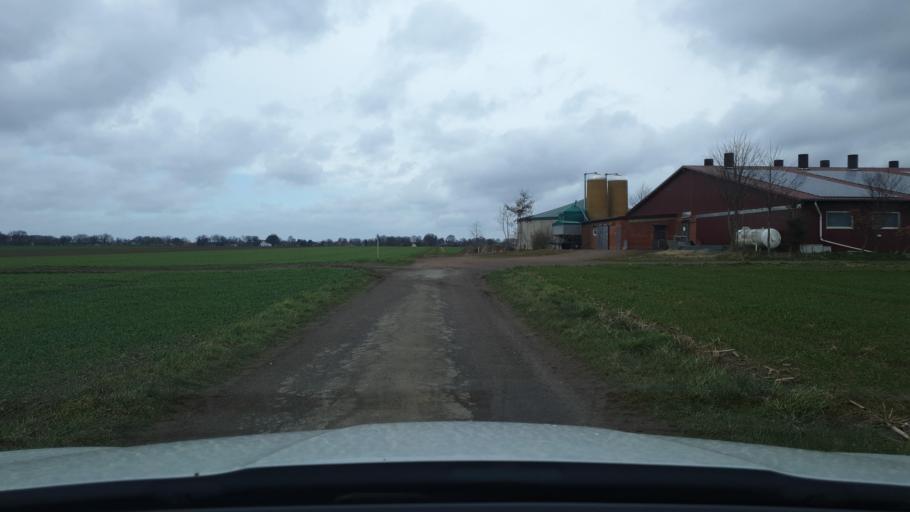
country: DE
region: North Rhine-Westphalia
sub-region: Regierungsbezirk Detmold
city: Hille
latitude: 52.3246
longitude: 8.8020
